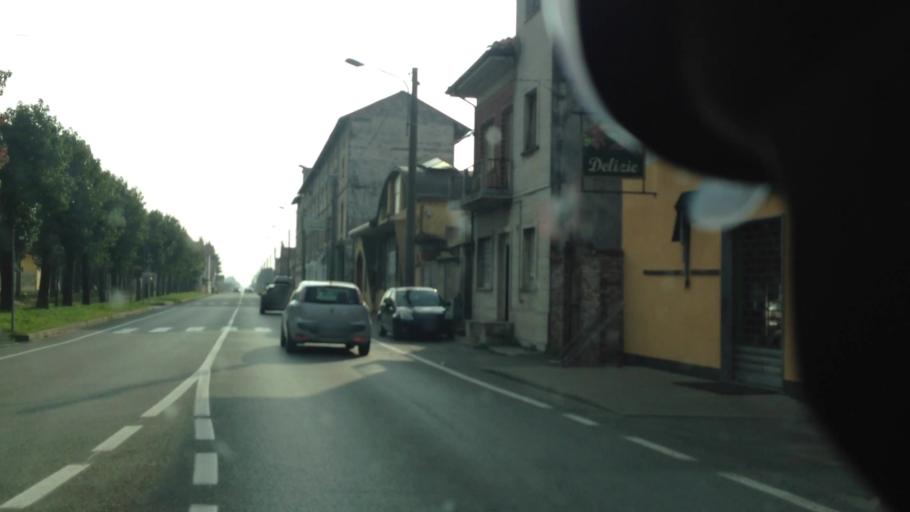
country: IT
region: Piedmont
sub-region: Provincia di Vercelli
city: Borgo d'Ale
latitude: 45.3457
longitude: 8.0499
